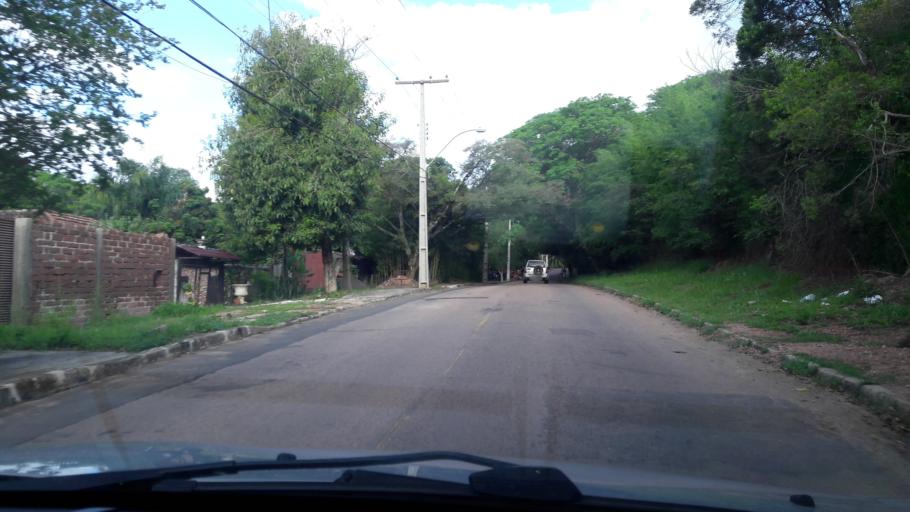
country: BR
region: Rio Grande do Sul
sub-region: Porto Alegre
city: Porto Alegre
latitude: -30.0847
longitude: -51.2033
